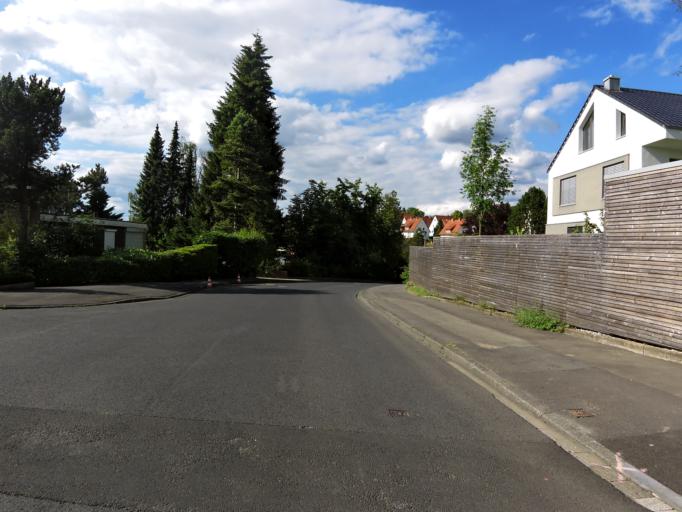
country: DE
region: Lower Saxony
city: Goettingen
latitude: 51.5121
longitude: 9.9622
